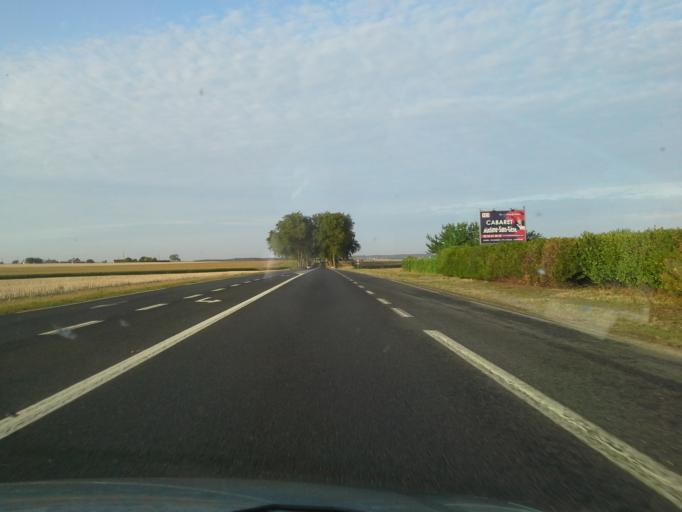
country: FR
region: Centre
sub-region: Departement du Loir-et-Cher
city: Naveil
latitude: 47.7611
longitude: 1.0510
